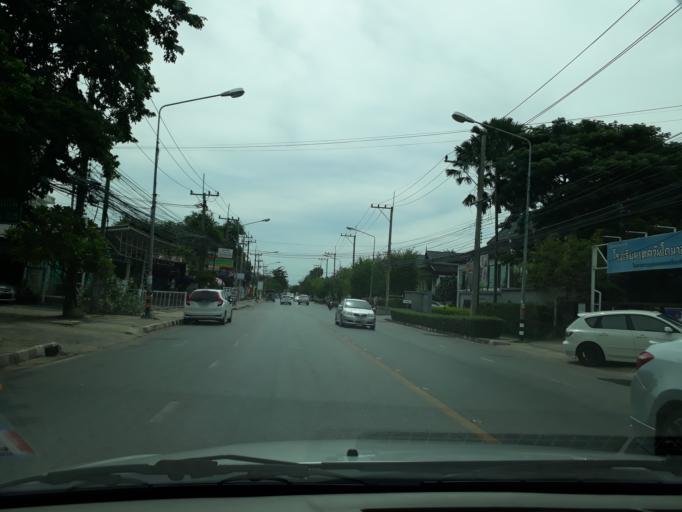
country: TH
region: Khon Kaen
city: Khon Kaen
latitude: 16.4366
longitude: 102.8475
